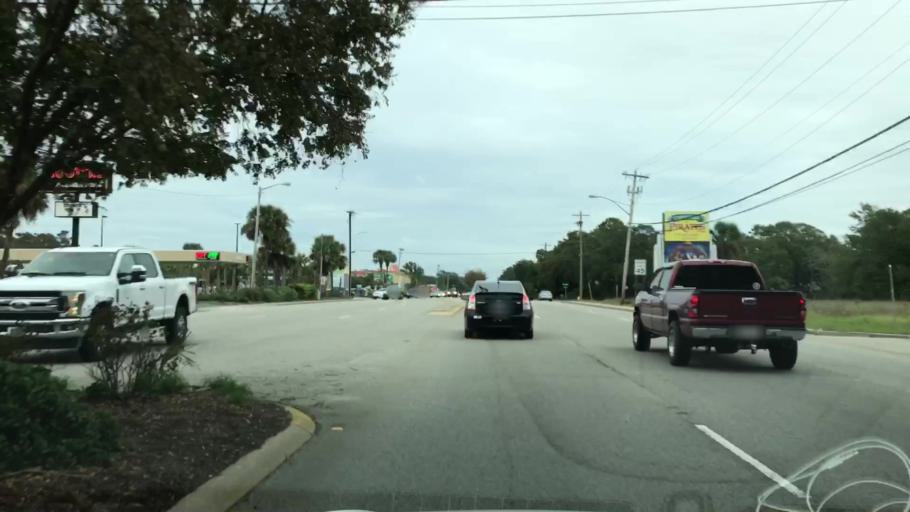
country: US
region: South Carolina
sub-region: Horry County
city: Myrtle Beach
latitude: 33.7160
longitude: -78.8557
